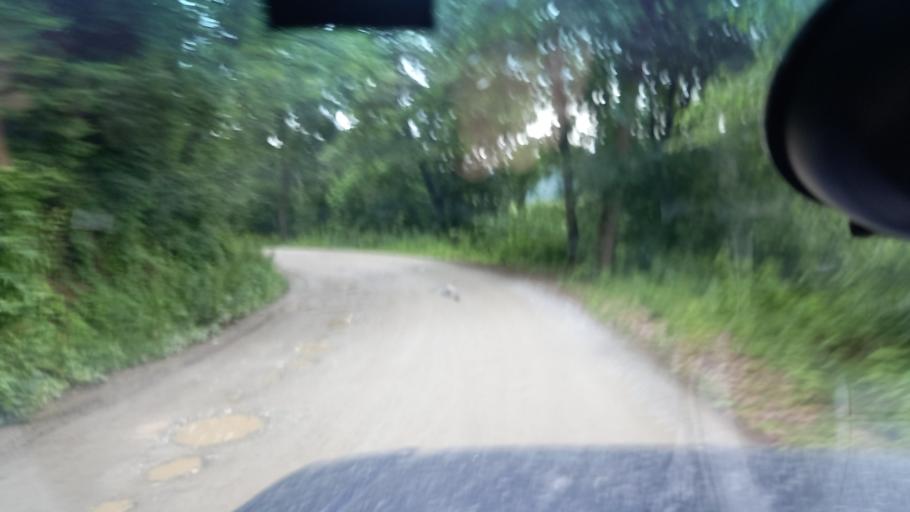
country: RU
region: Krasnodarskiy
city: Psebay
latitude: 44.0328
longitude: 40.7447
